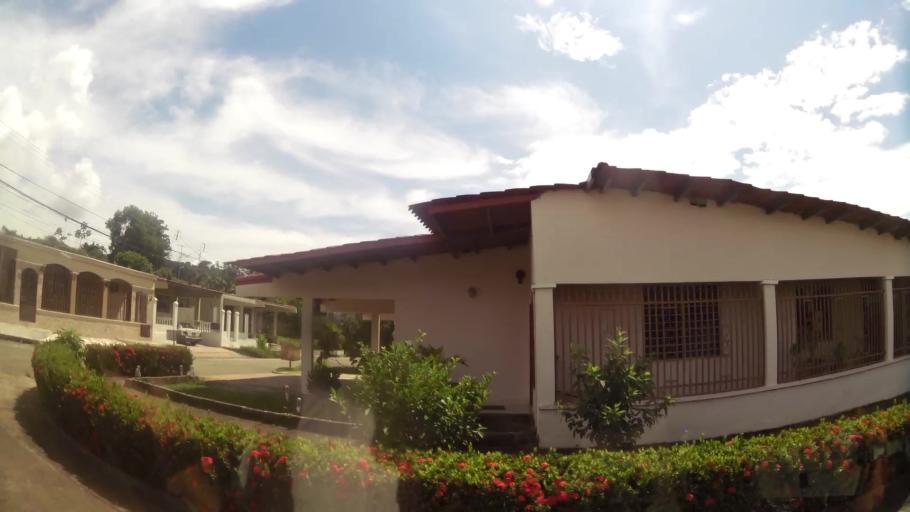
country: PA
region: Panama
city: San Vicente de Bique
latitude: 8.9211
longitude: -79.6915
